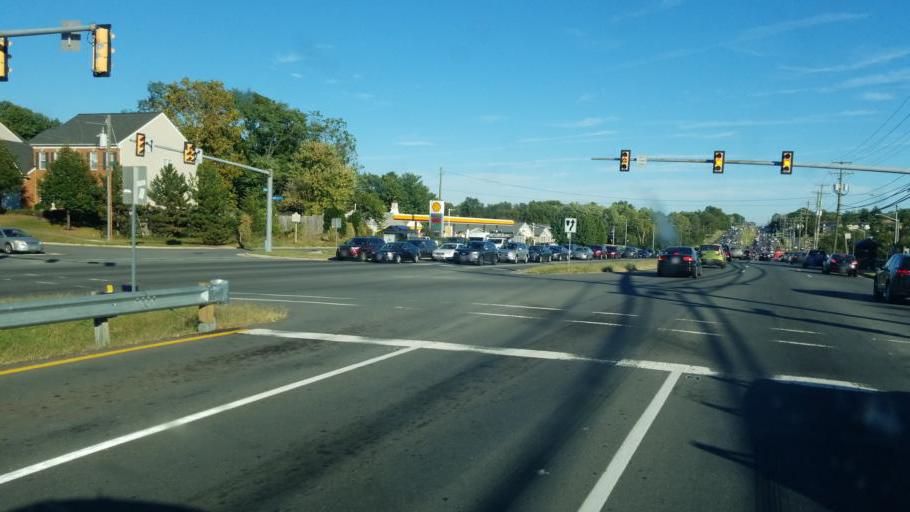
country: US
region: Virginia
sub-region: Fairfax County
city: Chantilly
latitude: 38.8908
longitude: -77.4230
